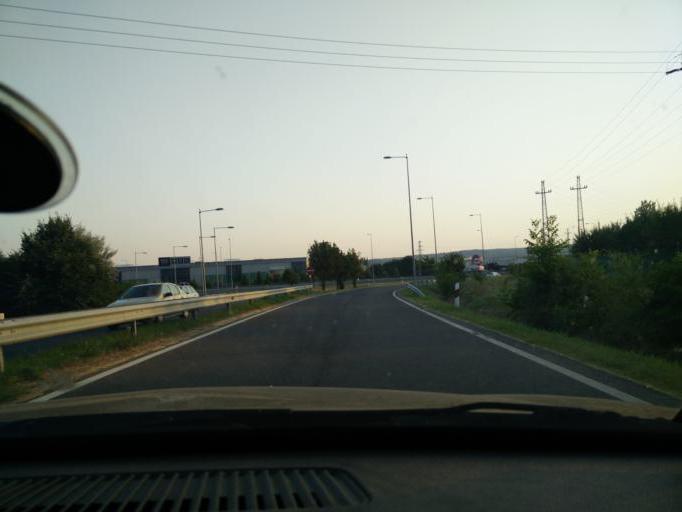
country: HU
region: Pest
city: Toeroekbalint
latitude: 47.4553
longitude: 18.9065
